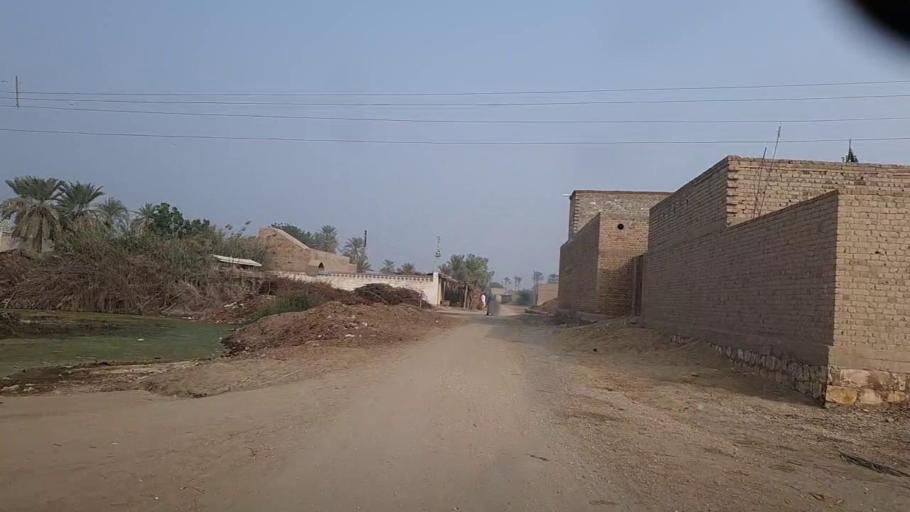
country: PK
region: Sindh
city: Bozdar
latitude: 27.1458
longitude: 68.6517
